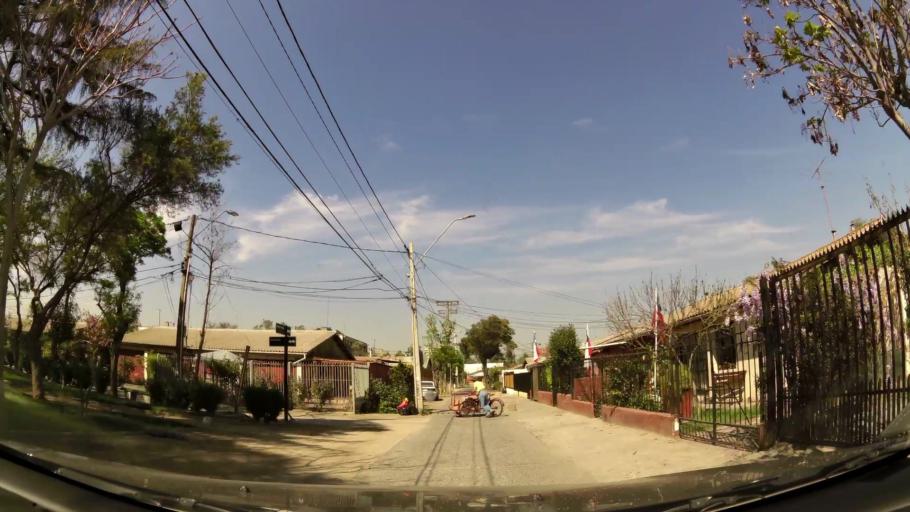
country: CL
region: Santiago Metropolitan
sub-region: Provincia de Maipo
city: San Bernardo
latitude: -33.5888
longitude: -70.6998
